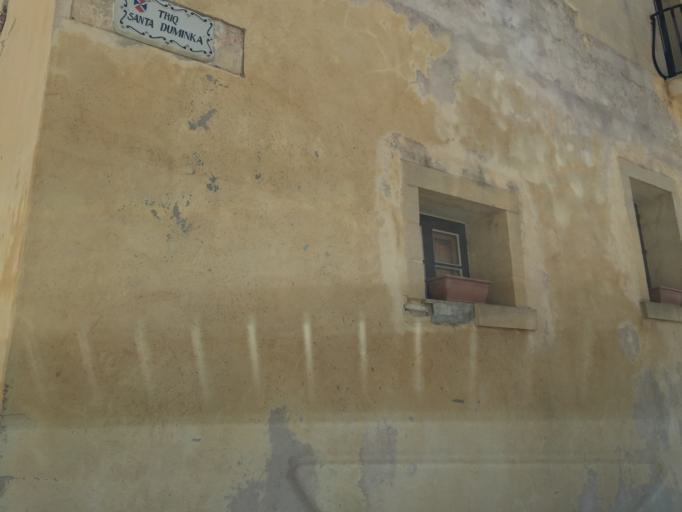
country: MT
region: Dingli
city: Dingli
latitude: 35.8629
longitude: 14.3851
